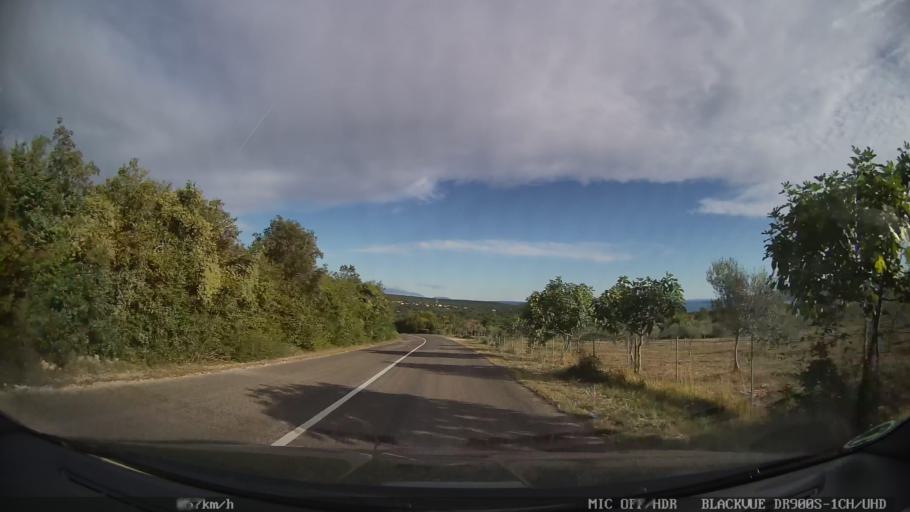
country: HR
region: Primorsko-Goranska
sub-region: Grad Krk
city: Krk
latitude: 45.0621
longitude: 14.4772
